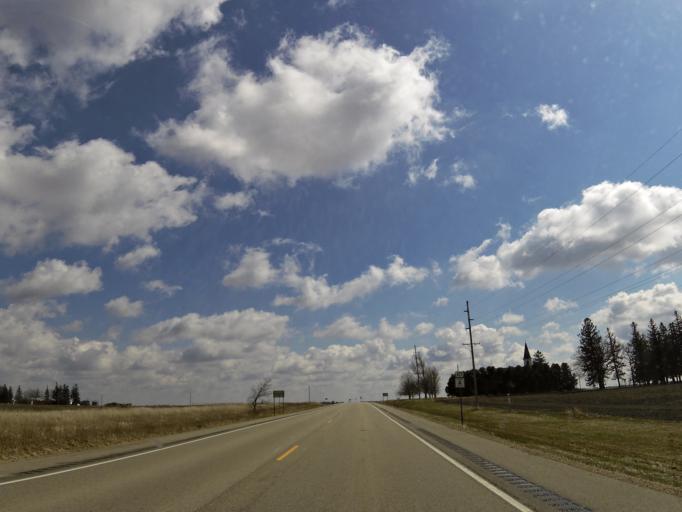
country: US
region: Minnesota
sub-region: Goodhue County
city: Kenyon
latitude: 44.1996
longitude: -92.9257
